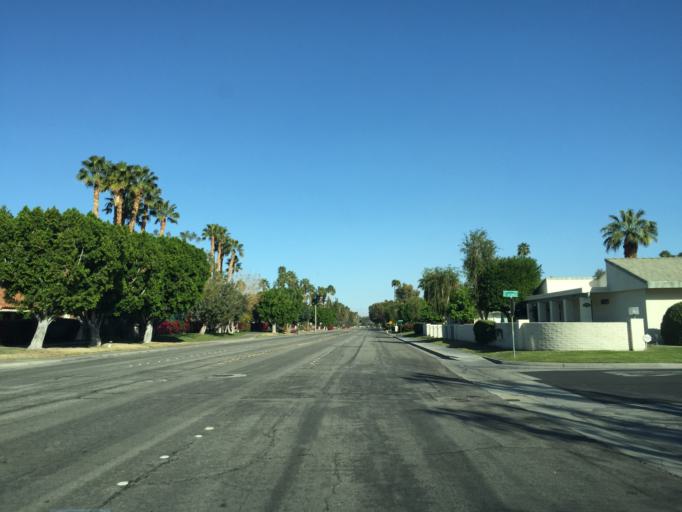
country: US
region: California
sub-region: Riverside County
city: Palm Springs
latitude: 33.8086
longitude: -116.5267
